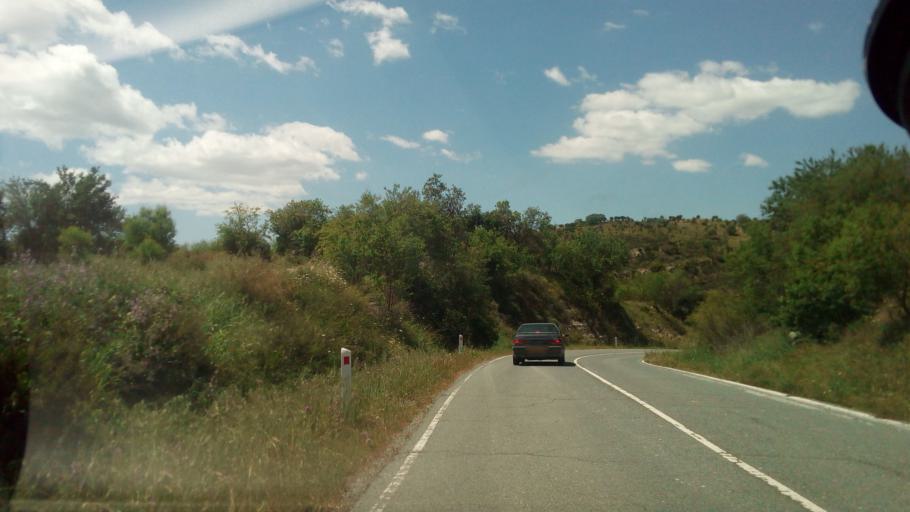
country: CY
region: Limassol
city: Pachna
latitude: 34.8150
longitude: 32.7814
